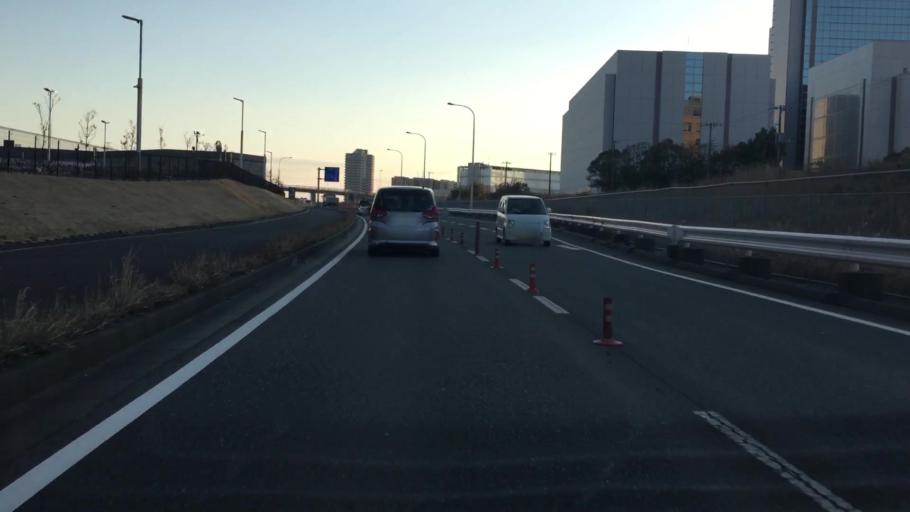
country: JP
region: Chiba
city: Shiroi
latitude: 35.8071
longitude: 140.1225
